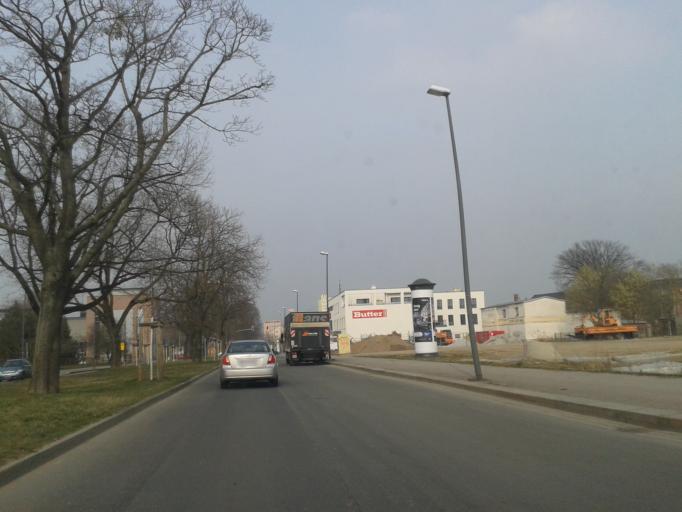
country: DE
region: Saxony
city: Dresden
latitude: 51.0424
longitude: 13.7807
